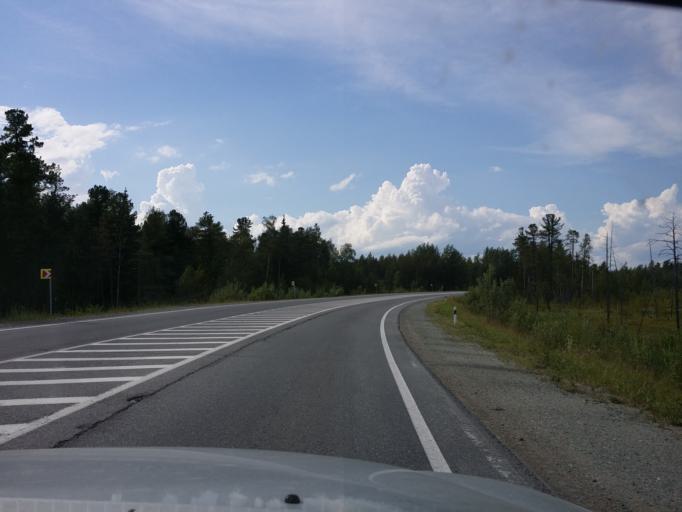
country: RU
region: Khanty-Mansiyskiy Avtonomnyy Okrug
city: Megion
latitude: 61.1007
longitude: 75.8595
